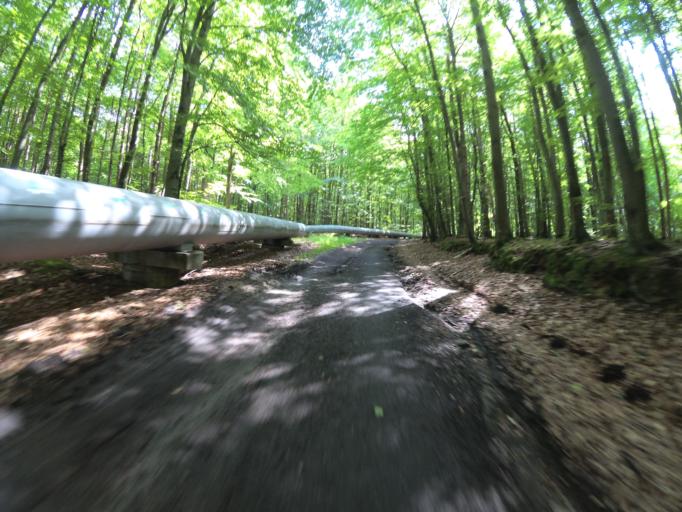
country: PL
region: Pomeranian Voivodeship
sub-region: Gdynia
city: Wielki Kack
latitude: 54.5064
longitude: 18.4911
